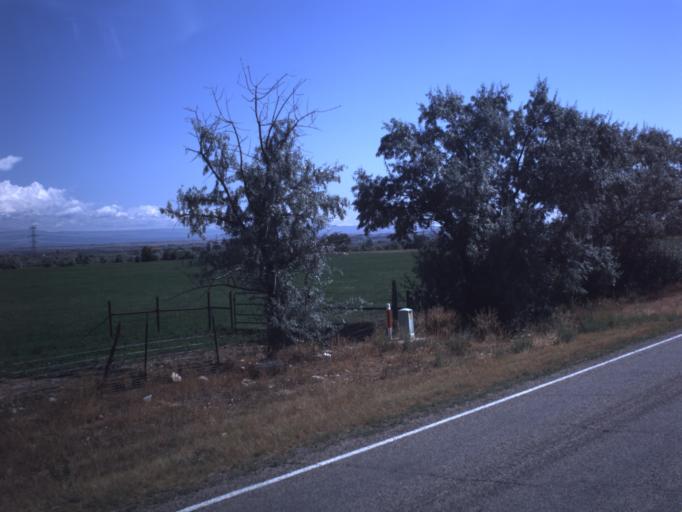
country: US
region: Utah
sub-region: Duchesne County
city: Roosevelt
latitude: 40.2585
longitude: -110.0921
